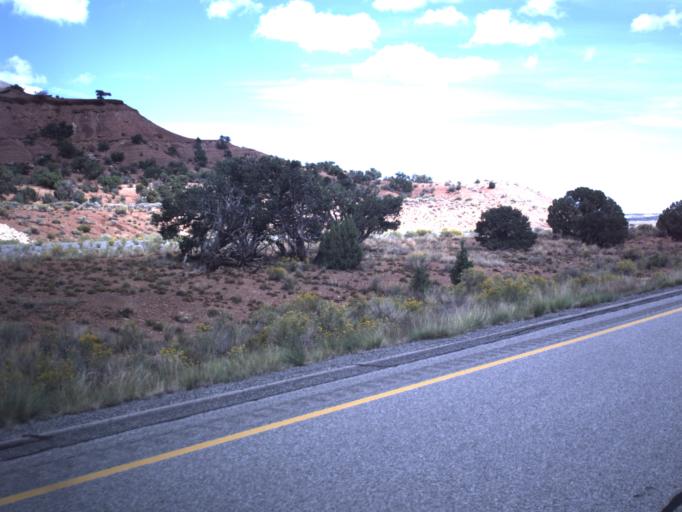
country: US
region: Utah
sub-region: Emery County
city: Castle Dale
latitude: 38.8673
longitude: -110.7151
